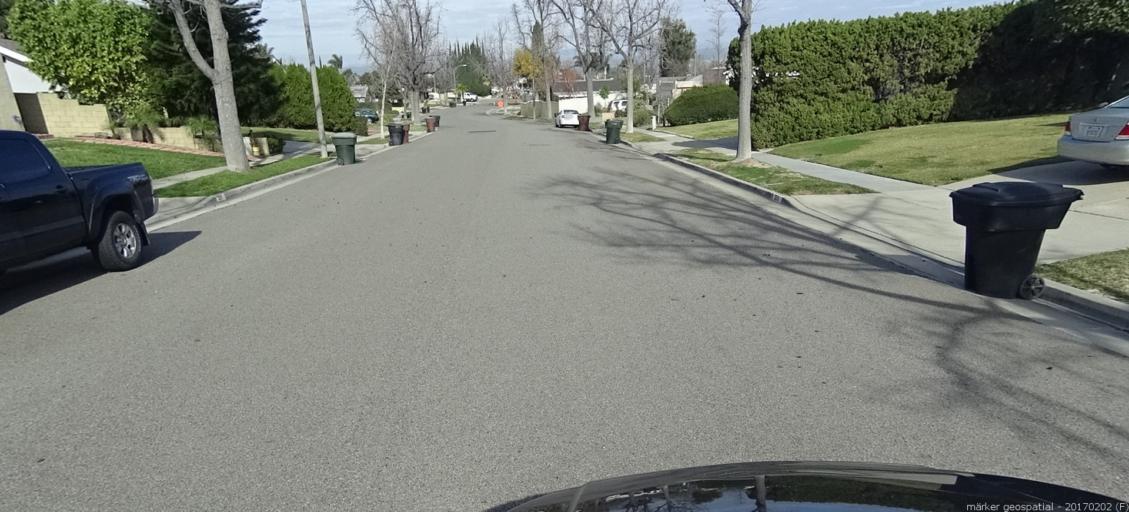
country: US
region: California
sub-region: Orange County
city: Villa Park
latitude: 33.8496
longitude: -117.8200
